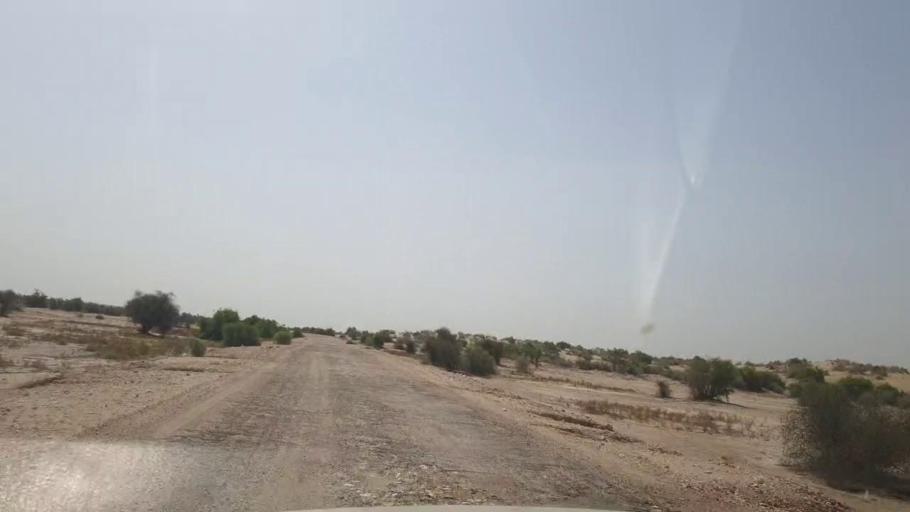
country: PK
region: Sindh
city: Rohri
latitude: 27.4365
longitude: 69.2459
